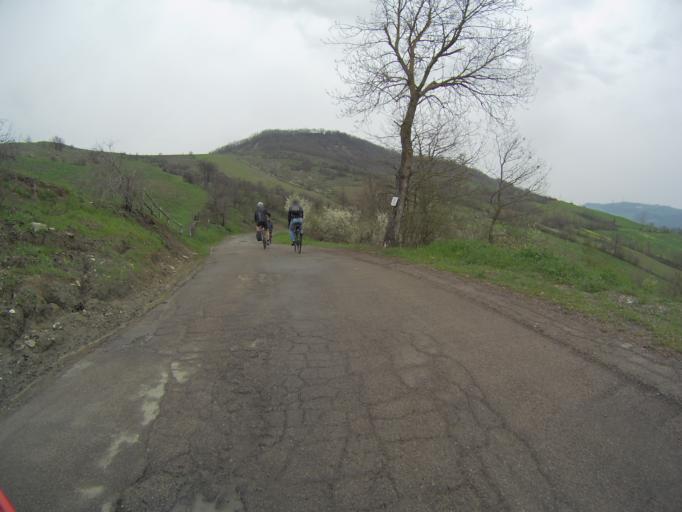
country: IT
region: Emilia-Romagna
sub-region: Provincia di Reggio Emilia
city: Casina
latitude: 44.5371
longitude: 10.4483
